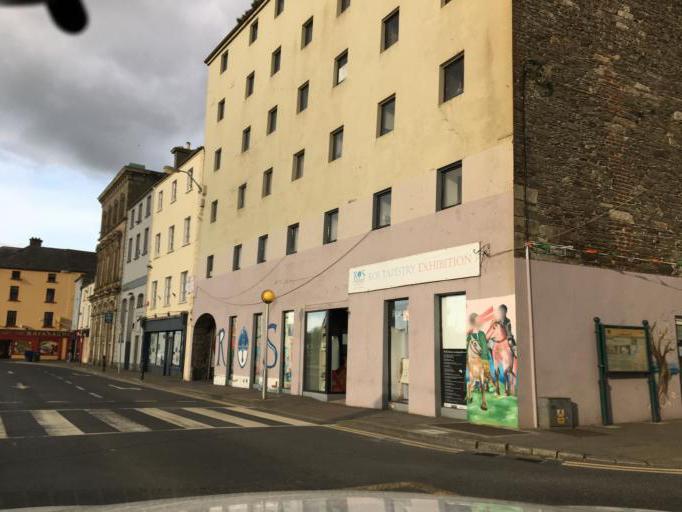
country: IE
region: Leinster
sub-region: Loch Garman
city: New Ross
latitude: 52.3953
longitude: -6.9457
